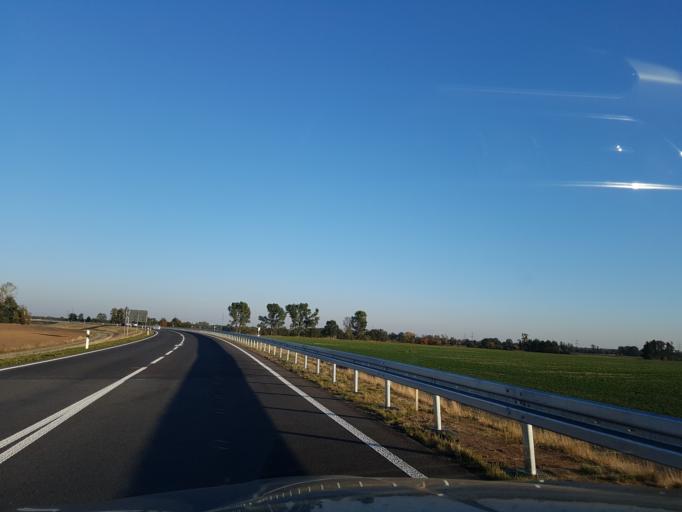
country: DE
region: Brandenburg
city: Bad Liebenwerda
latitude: 51.5034
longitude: 13.3923
